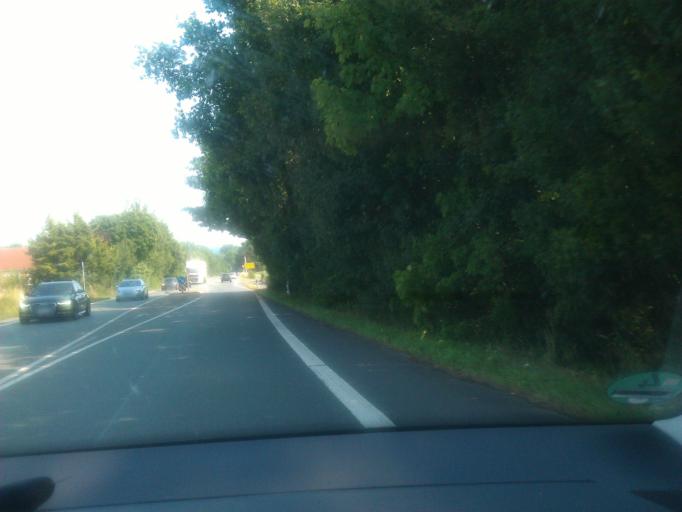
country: DE
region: North Rhine-Westphalia
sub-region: Regierungsbezirk Detmold
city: Lemgo
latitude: 52.0337
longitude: 8.8419
